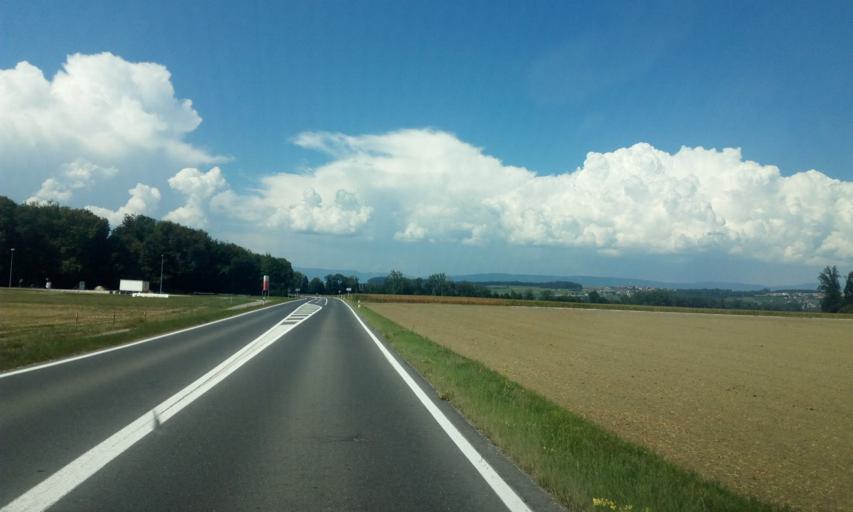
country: CH
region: Vaud
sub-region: Broye-Vully District
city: Avenches
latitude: 46.8852
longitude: 7.0223
